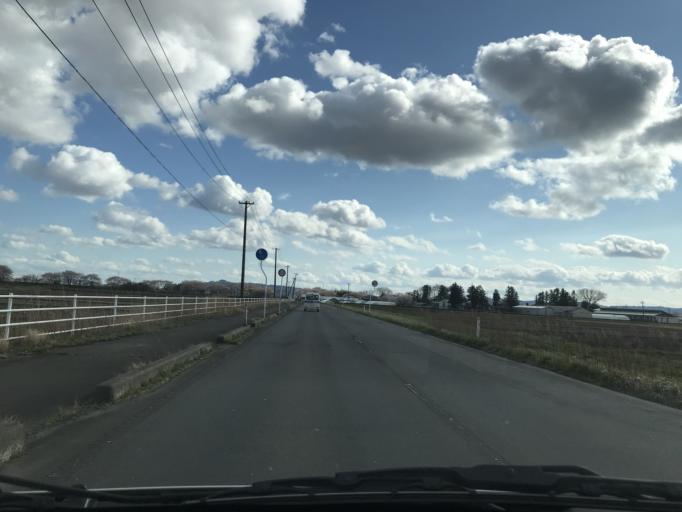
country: JP
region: Miyagi
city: Wakuya
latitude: 38.6470
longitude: 141.1901
